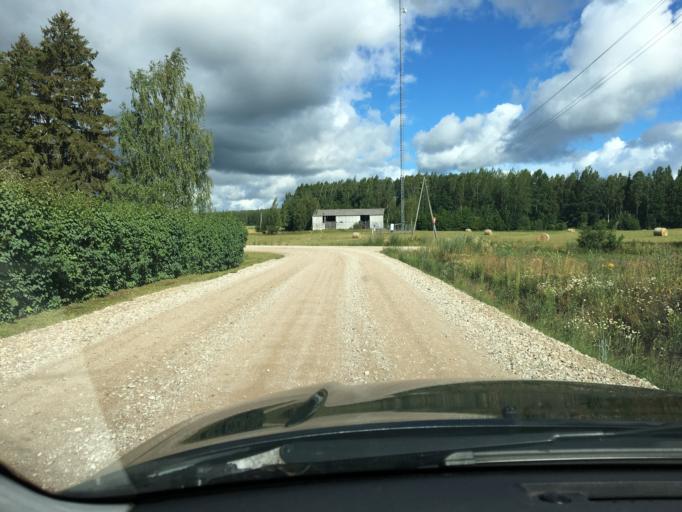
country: LV
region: Kuldigas Rajons
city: Kuldiga
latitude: 56.8427
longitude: 21.9349
